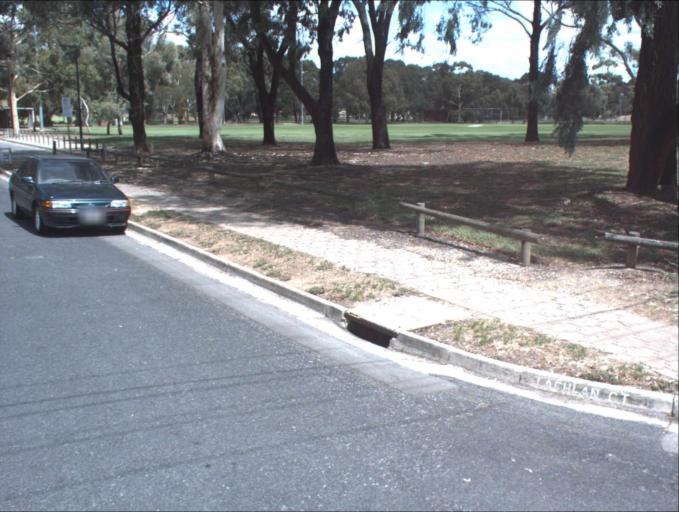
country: AU
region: South Australia
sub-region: Port Adelaide Enfield
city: Gilles Plains
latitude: -34.8418
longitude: 138.6659
